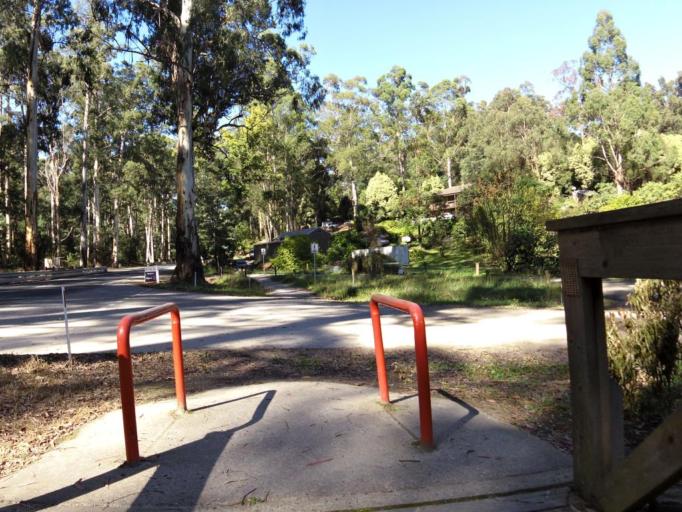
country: AU
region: Victoria
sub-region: Cardinia
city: Cockatoo
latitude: -37.9419
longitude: 145.4934
